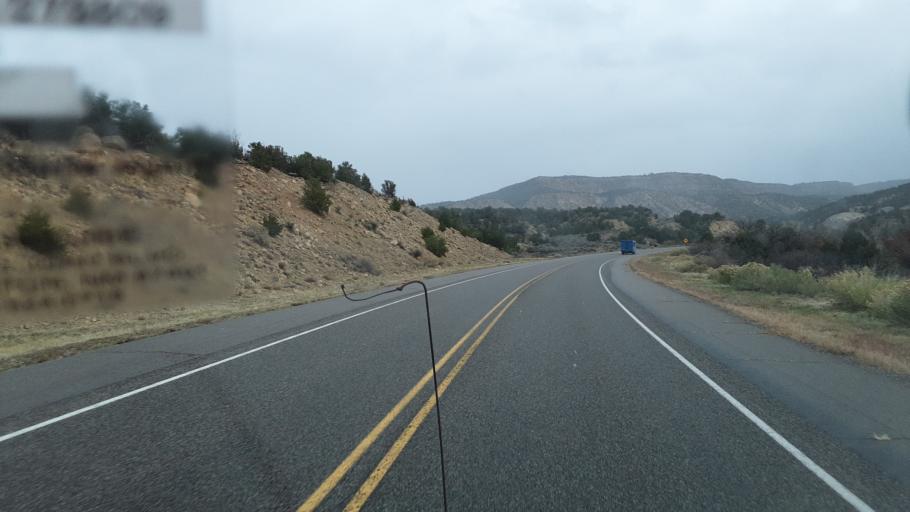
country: US
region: New Mexico
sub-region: Rio Arriba County
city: Santa Teresa
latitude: 36.3859
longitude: -106.5013
